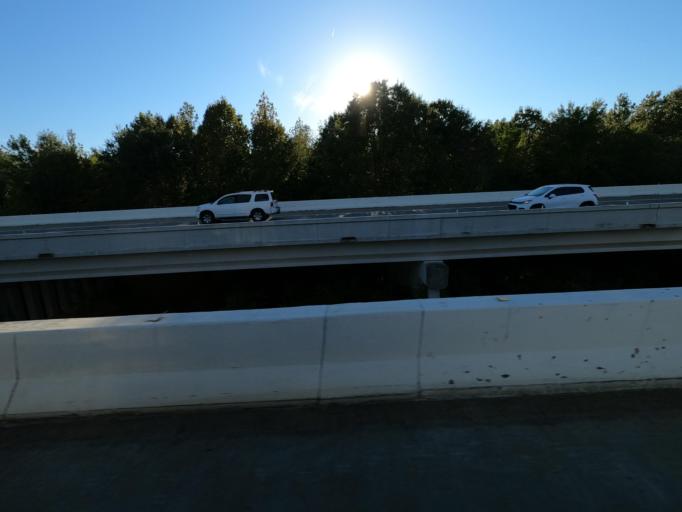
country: US
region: Tennessee
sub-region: Shelby County
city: Arlington
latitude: 35.2947
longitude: -89.6919
